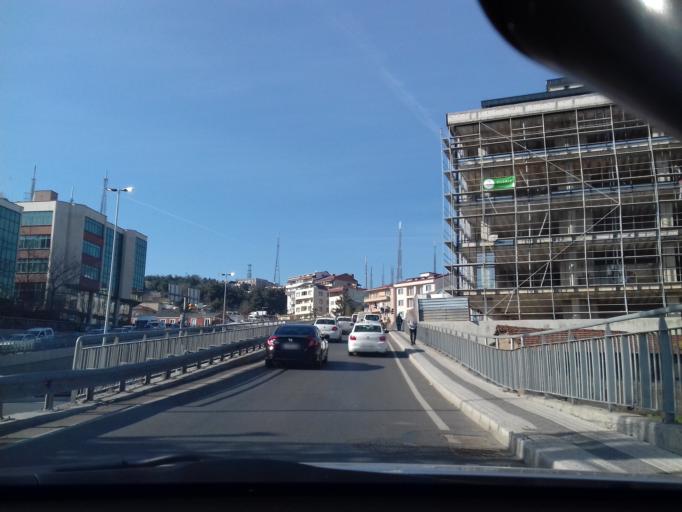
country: TR
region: Istanbul
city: Umraniye
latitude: 41.0216
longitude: 29.0747
